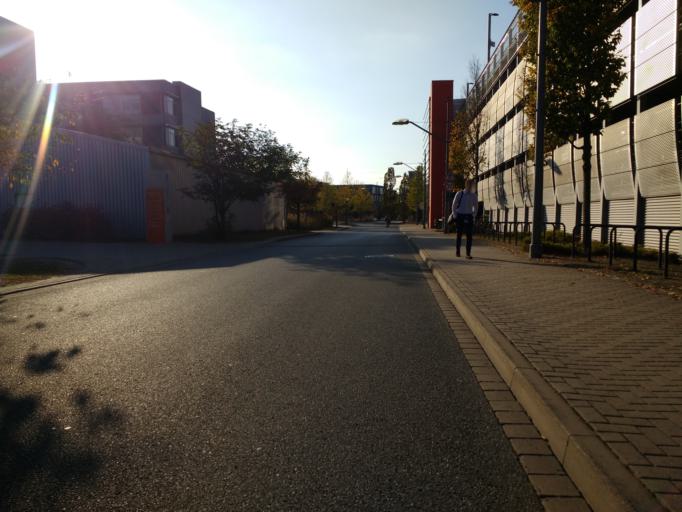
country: DE
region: Lower Saxony
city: Wolfsburg
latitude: 52.4250
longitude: 10.7451
